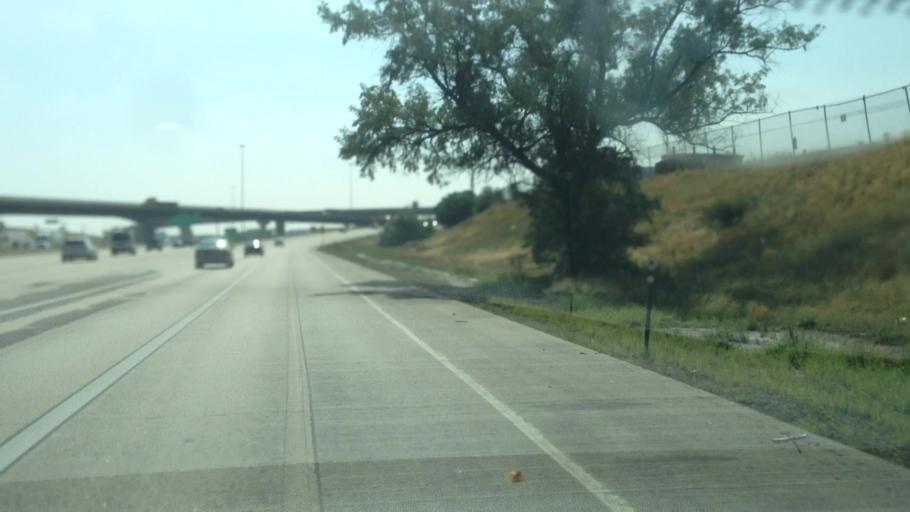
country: US
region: Colorado
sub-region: Adams County
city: Aurora
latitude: 39.7728
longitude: -104.8338
